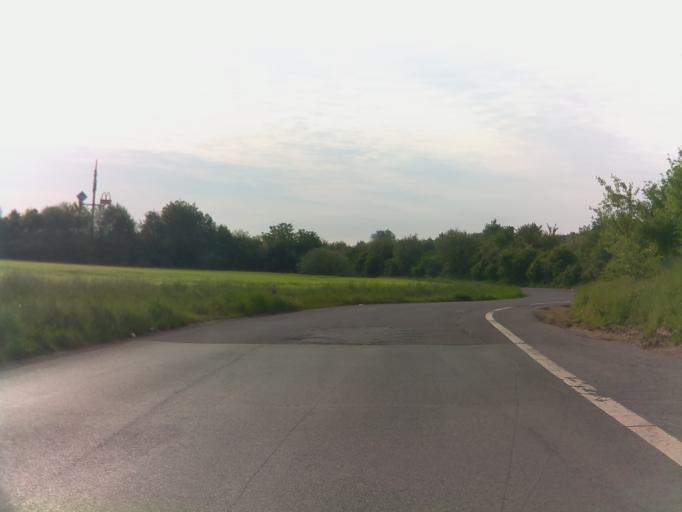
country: DE
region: Lower Saxony
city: Konigslutter am Elm
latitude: 52.3123
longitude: 10.8172
